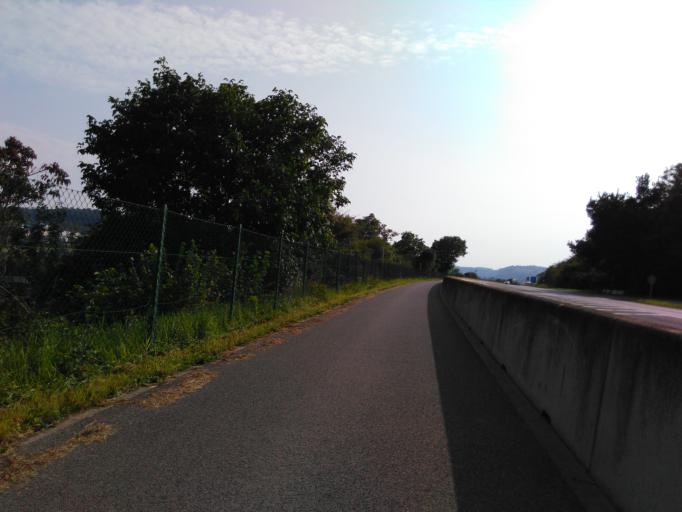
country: LU
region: Grevenmacher
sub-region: Canton de Grevenmacher
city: Mertert
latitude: 49.6970
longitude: 6.4692
